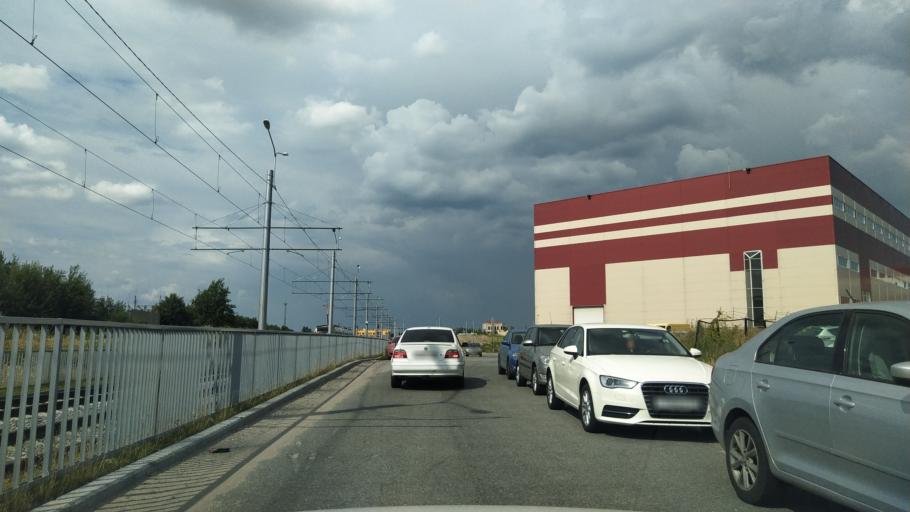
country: RU
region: St.-Petersburg
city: Krasnogvargeisky
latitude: 59.9685
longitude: 30.4632
